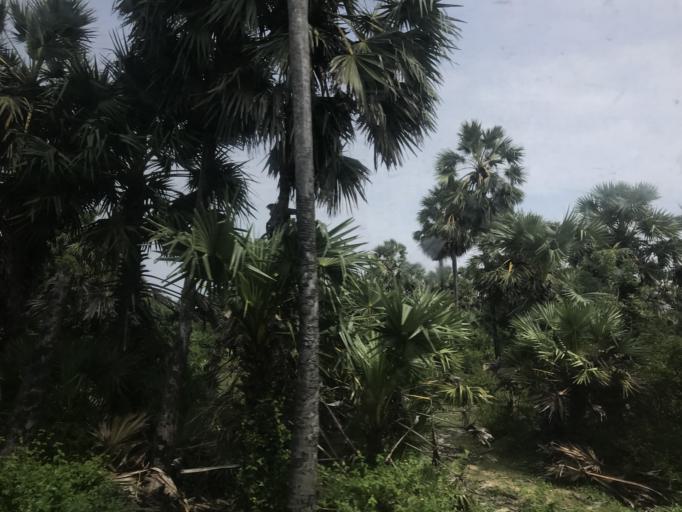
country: LK
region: Northern Province
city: Kilinochchi
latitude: 9.5967
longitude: 80.3420
